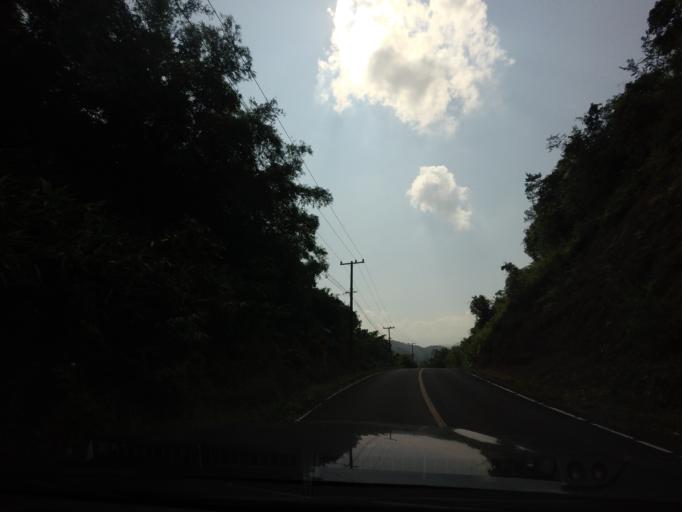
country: TH
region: Nan
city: Bo Kluea
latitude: 19.0493
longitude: 101.1682
